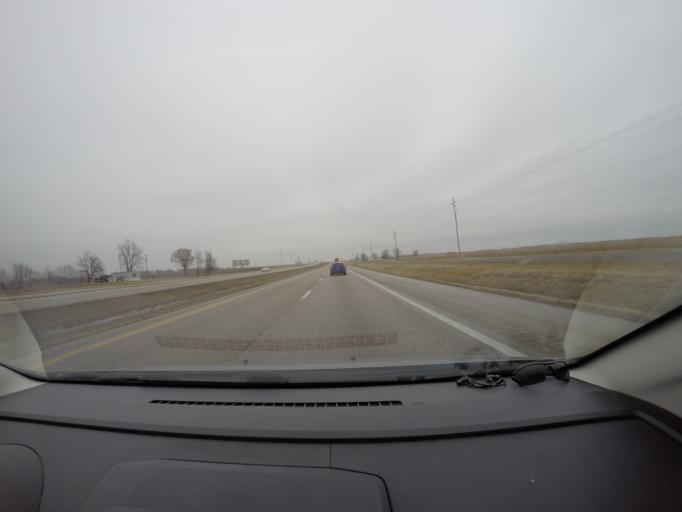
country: US
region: Missouri
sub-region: Montgomery County
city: Montgomery City
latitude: 38.8953
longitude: -91.4420
